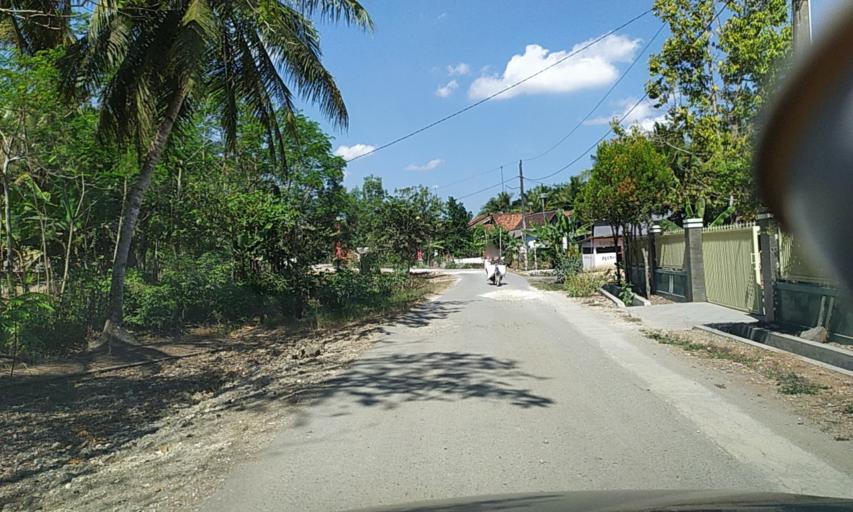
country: ID
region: Central Java
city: Kalenaren
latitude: -7.5808
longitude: 108.7979
